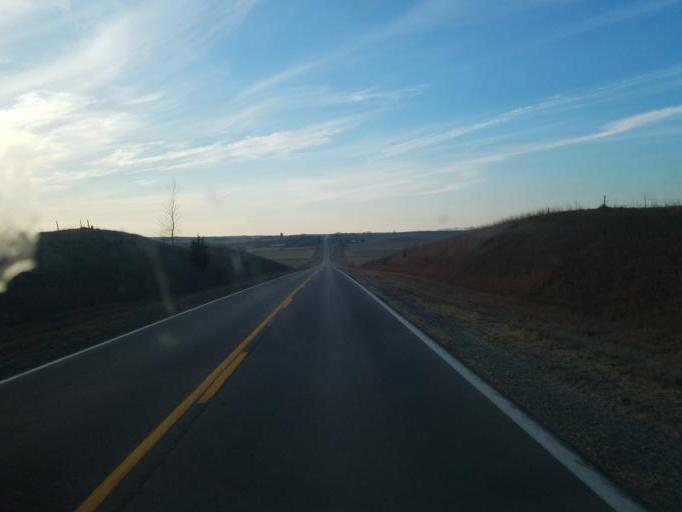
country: US
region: Nebraska
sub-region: Cedar County
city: Hartington
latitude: 42.7284
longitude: -97.3057
